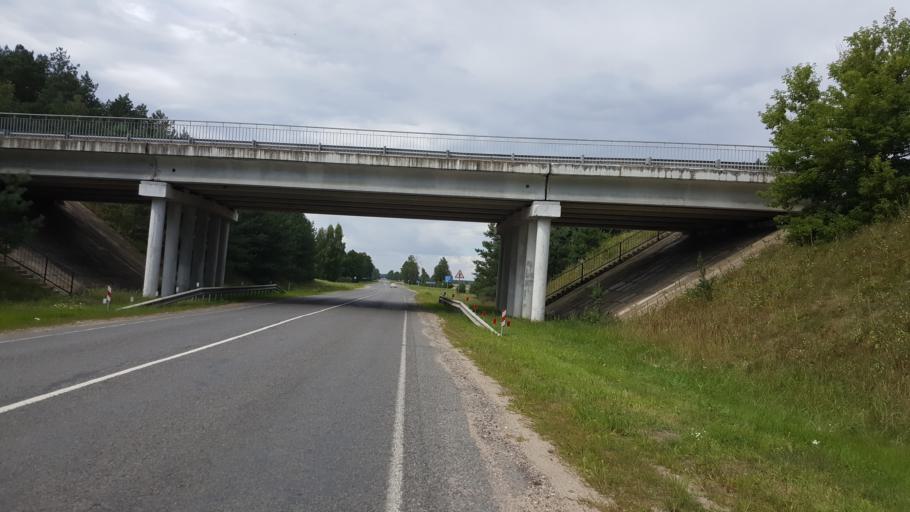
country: BY
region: Brest
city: Kamyanyets
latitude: 52.3418
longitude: 23.9068
